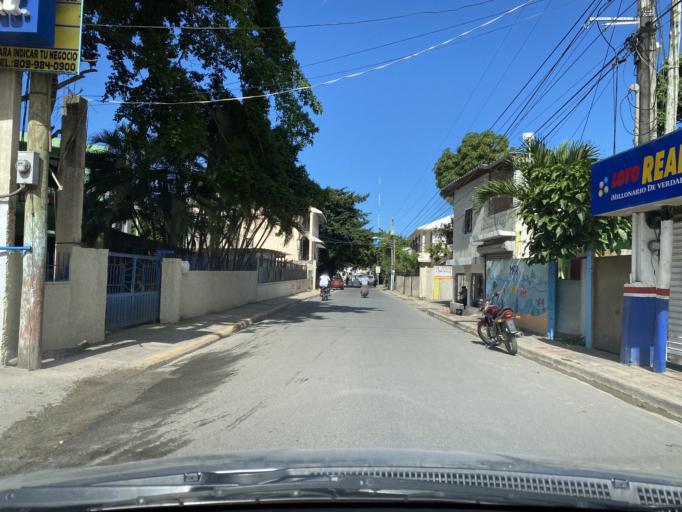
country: DO
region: Samana
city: Las Terrenas
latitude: 19.3114
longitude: -69.5423
